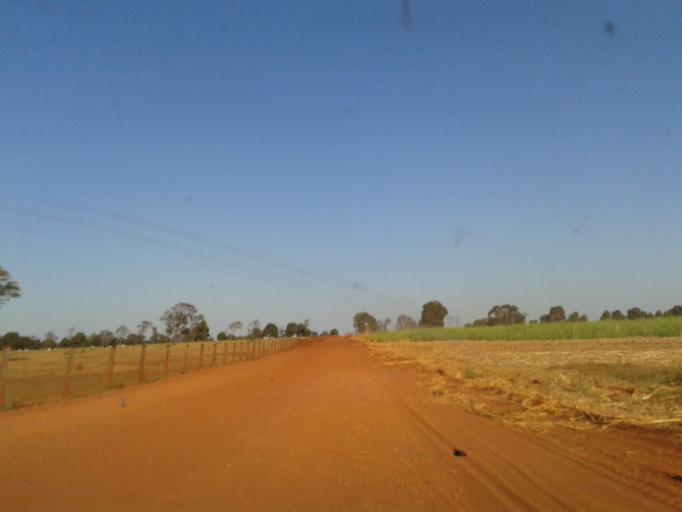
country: BR
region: Minas Gerais
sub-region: Santa Vitoria
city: Santa Vitoria
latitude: -18.8189
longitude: -50.1471
